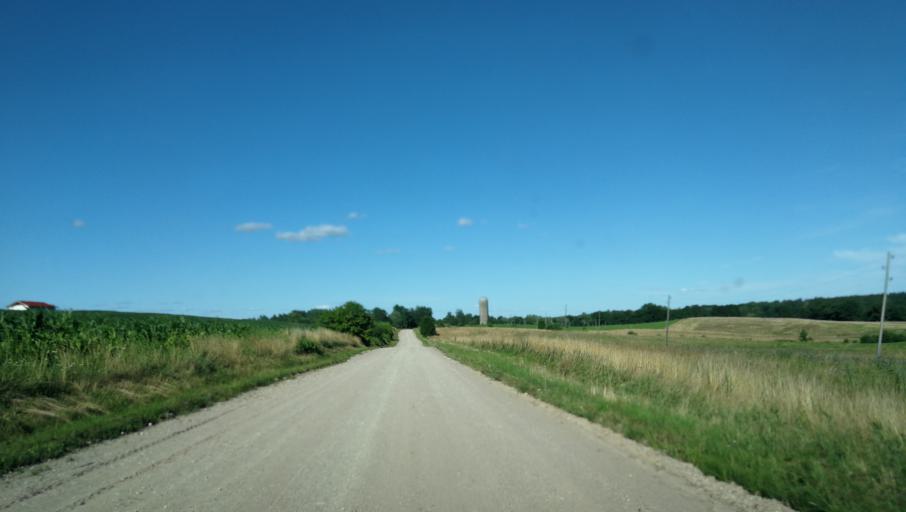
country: LV
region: Jaunpiebalga
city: Jaunpiebalga
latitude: 57.0107
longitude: 26.0438
